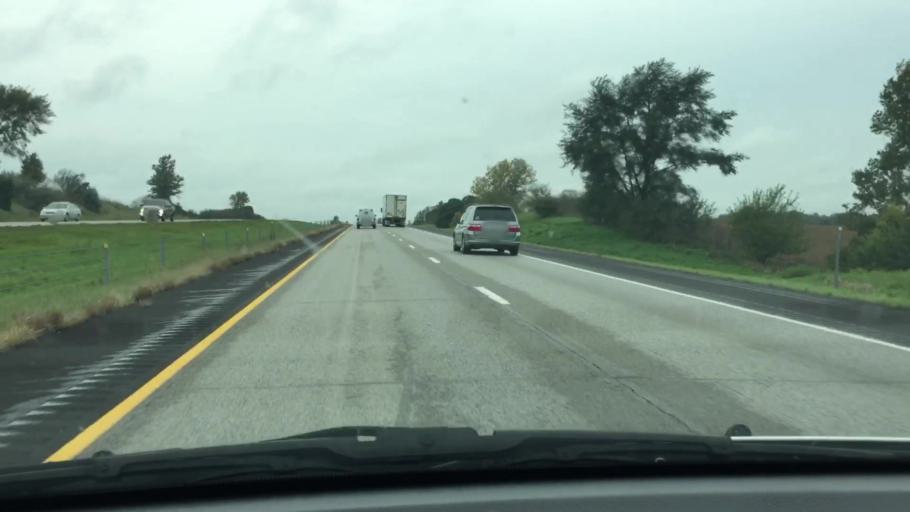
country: US
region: Iowa
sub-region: Johnson County
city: Tiffin
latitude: 41.6952
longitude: -91.7323
